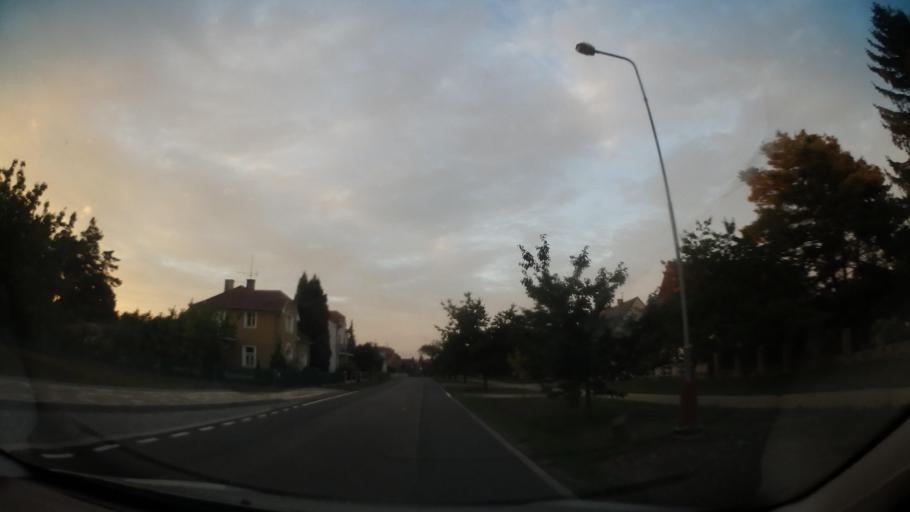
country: CZ
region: Central Bohemia
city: Loucen
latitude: 50.2810
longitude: 15.0170
